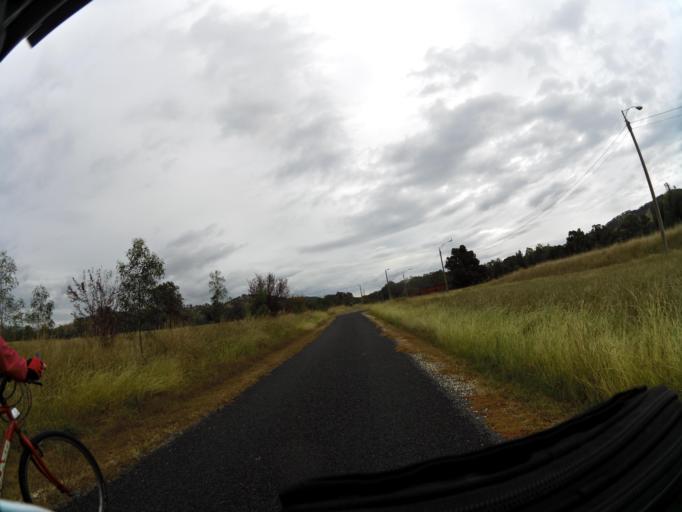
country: AU
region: Victoria
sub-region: Wodonga
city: Wodonga
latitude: -36.1505
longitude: 146.9398
